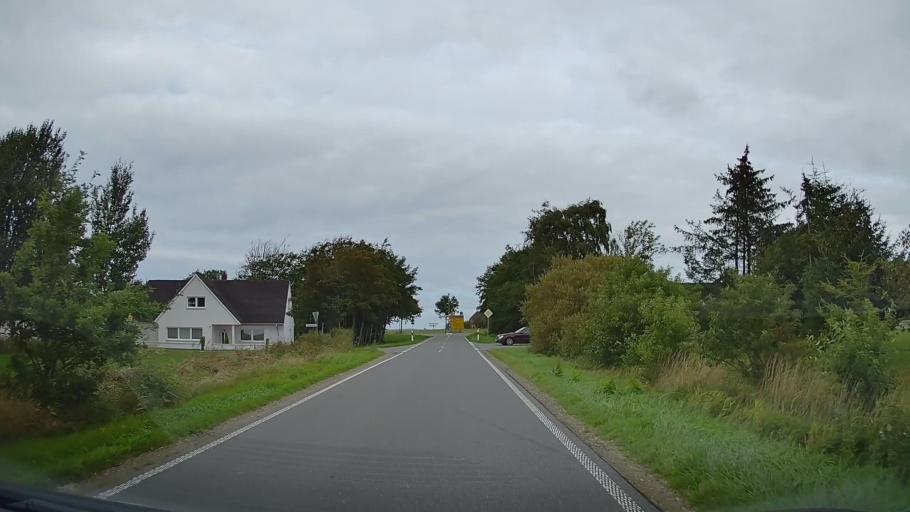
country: DE
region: Schleswig-Holstein
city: Aventoft
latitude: 54.8989
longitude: 8.8092
